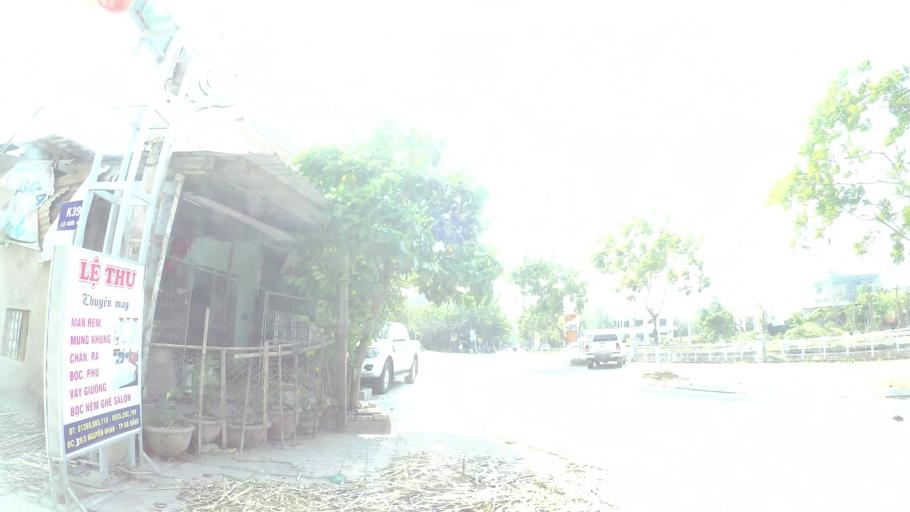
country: VN
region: Da Nang
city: Cam Le
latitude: 16.0119
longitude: 108.1987
